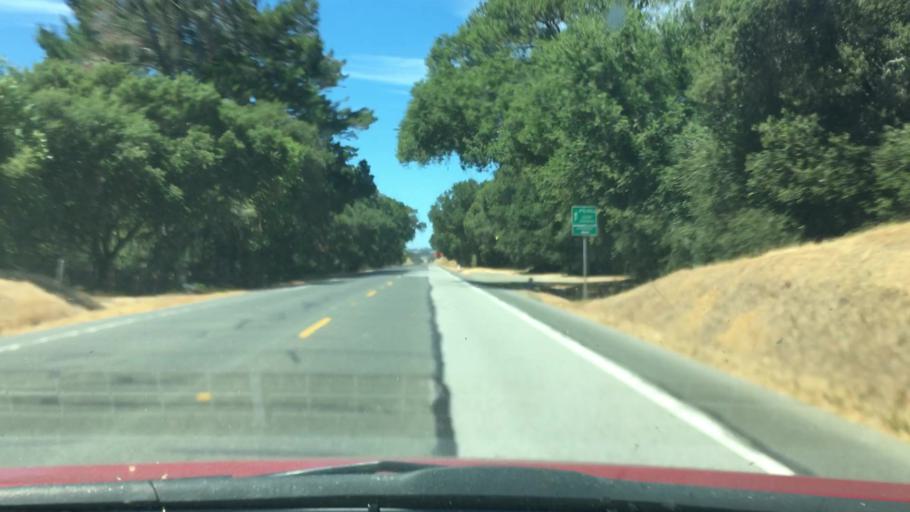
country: US
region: California
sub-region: San Mateo County
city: Emerald Lake Hills
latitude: 37.4679
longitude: -122.3016
